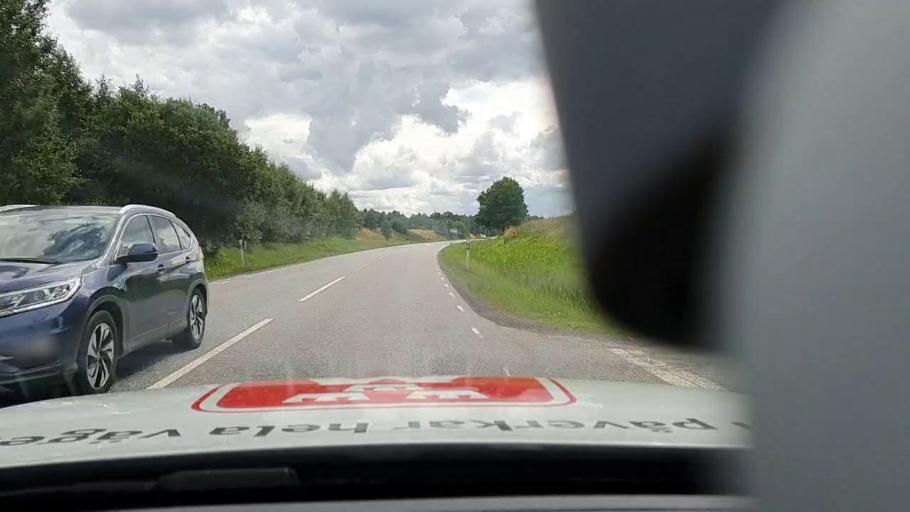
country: SE
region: Vaestra Goetaland
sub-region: Lidkopings Kommun
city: Lidkoping
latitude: 58.5397
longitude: 13.1131
